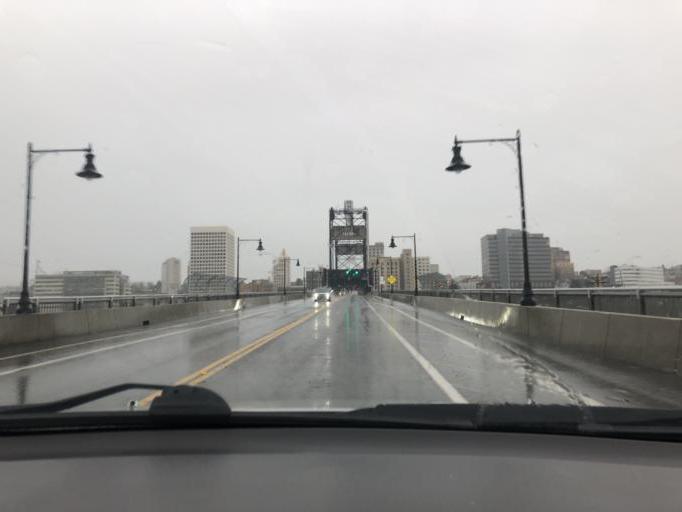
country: US
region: Washington
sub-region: Pierce County
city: Tacoma
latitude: 47.2543
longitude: -122.4300
